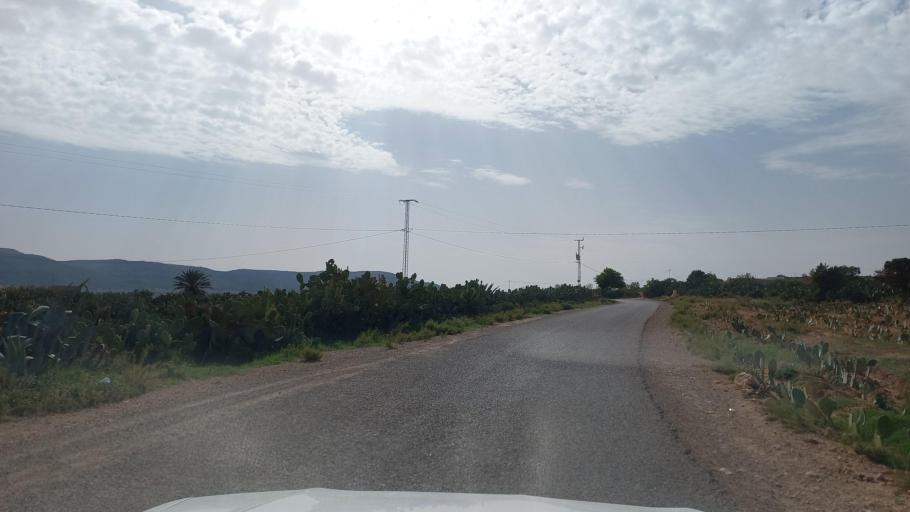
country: TN
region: Al Qasrayn
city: Kasserine
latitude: 35.3640
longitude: 8.8531
